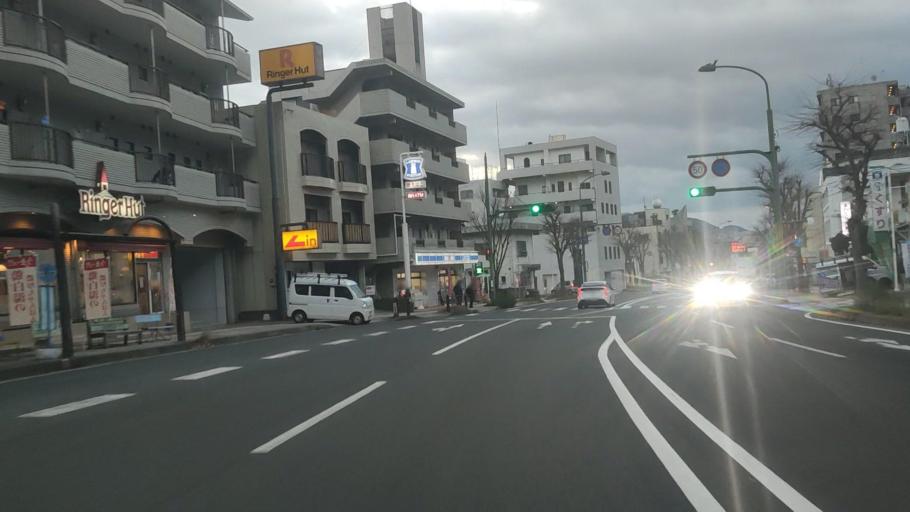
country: JP
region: Nagasaki
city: Nagasaki-shi
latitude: 32.7625
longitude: 129.8888
